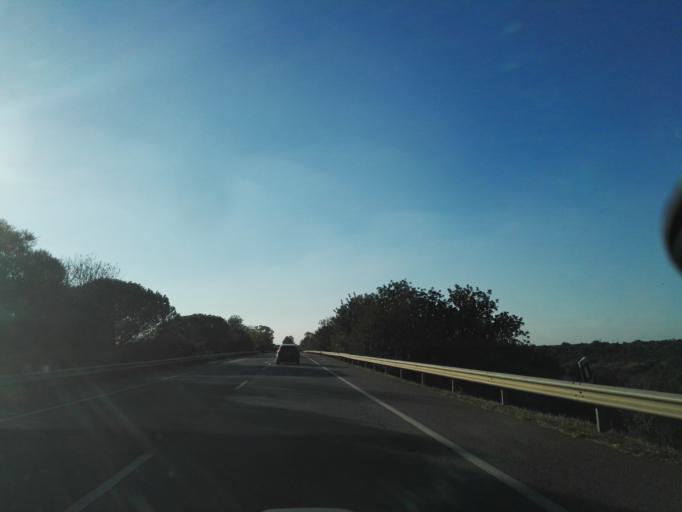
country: PT
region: Evora
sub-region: Estremoz
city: Estremoz
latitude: 38.8336
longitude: -7.5558
